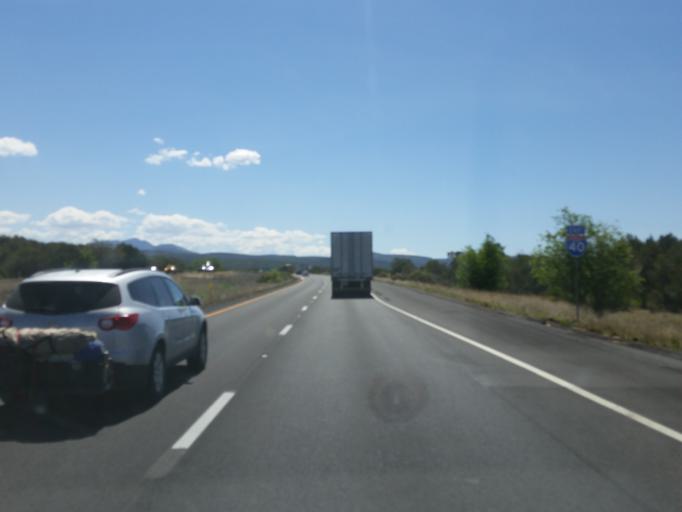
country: US
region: Arizona
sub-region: Coconino County
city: Williams
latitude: 35.2154
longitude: -112.4339
